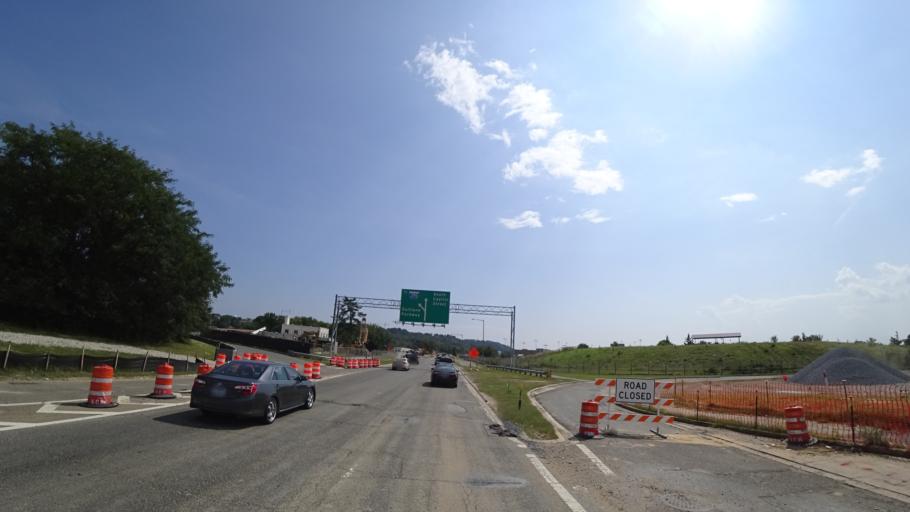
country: US
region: Washington, D.C.
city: Washington, D.C.
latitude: 38.8663
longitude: -77.0027
